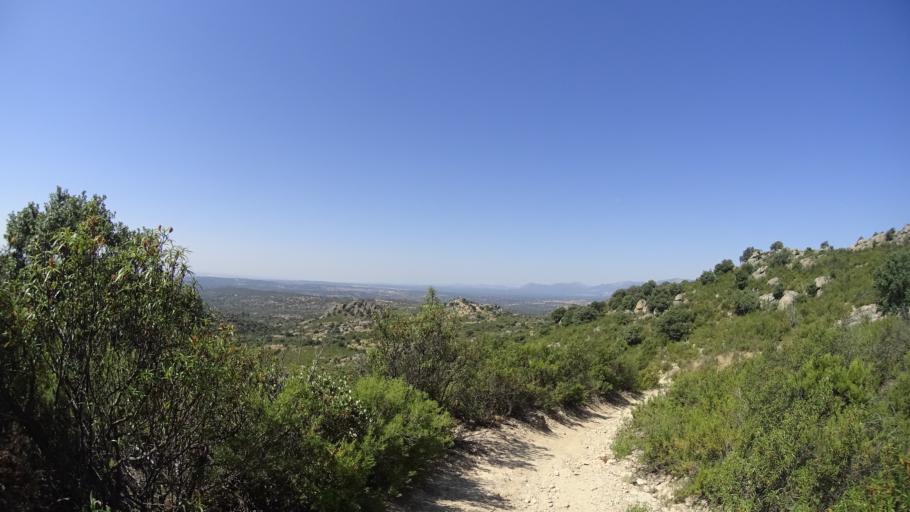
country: ES
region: Madrid
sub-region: Provincia de Madrid
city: Hoyo de Manzanares
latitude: 40.6401
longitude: -3.9409
